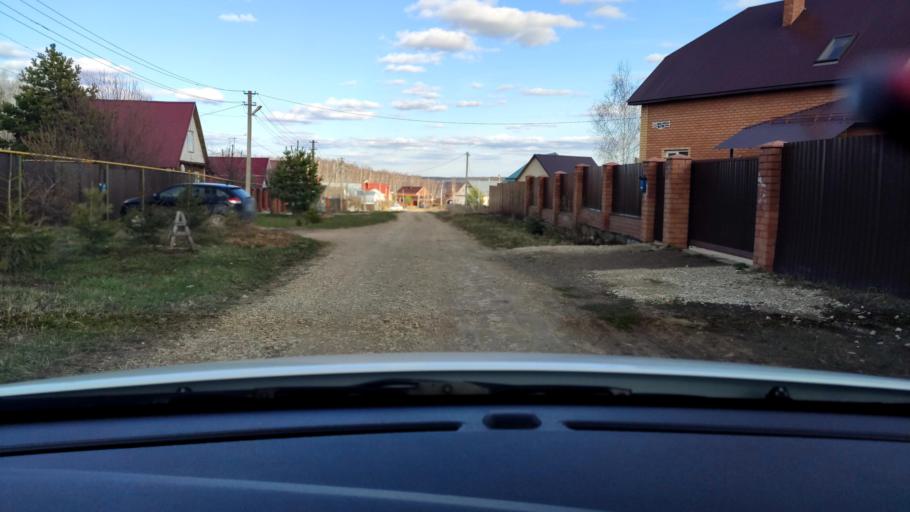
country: RU
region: Tatarstan
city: Vysokaya Gora
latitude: 55.8917
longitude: 49.3585
